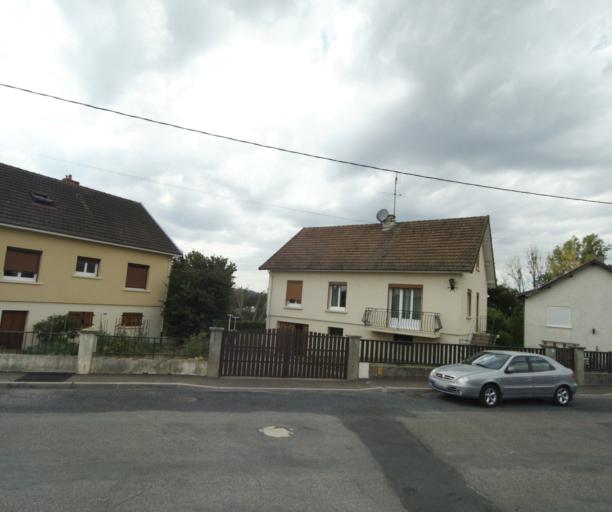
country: FR
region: Bourgogne
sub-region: Departement de Saone-et-Loire
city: Gueugnon
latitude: 46.6046
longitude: 4.0748
